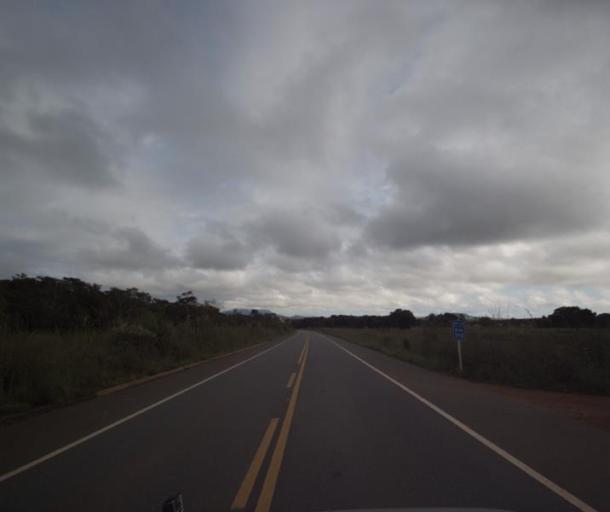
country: BR
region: Goias
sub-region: Padre Bernardo
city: Padre Bernardo
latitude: -15.3192
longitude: -48.6577
